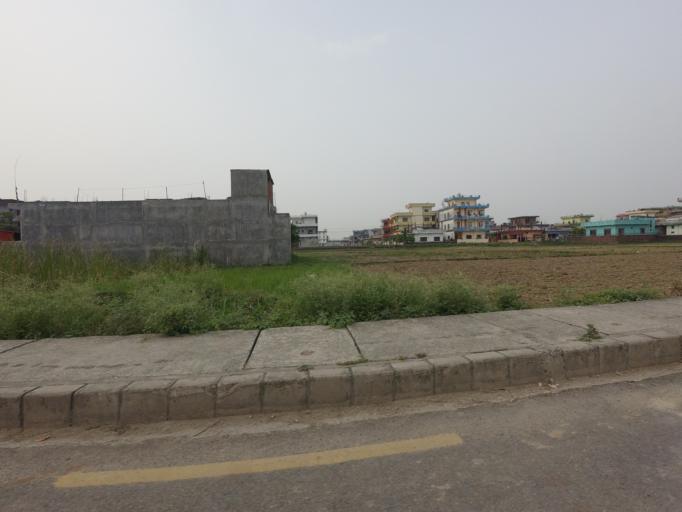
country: NP
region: Western Region
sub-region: Lumbini Zone
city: Bhairahawa
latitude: 27.5214
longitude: 83.4468
